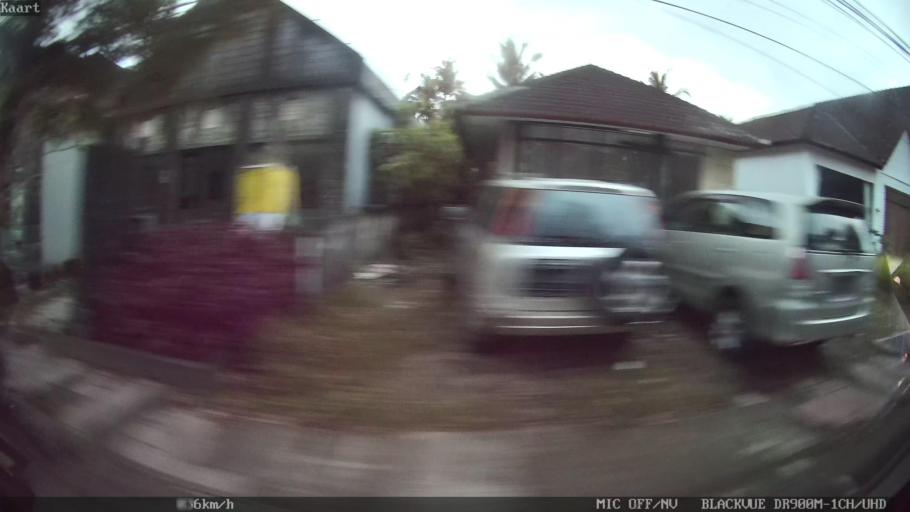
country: ID
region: Bali
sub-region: Kabupaten Gianyar
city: Ubud
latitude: -8.4910
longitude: 115.2537
